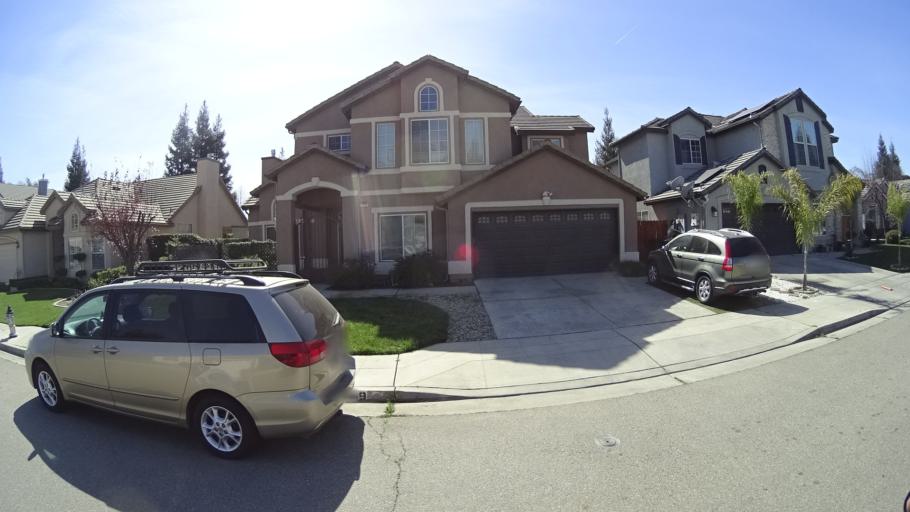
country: US
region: California
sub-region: Fresno County
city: Clovis
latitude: 36.8944
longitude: -119.7627
